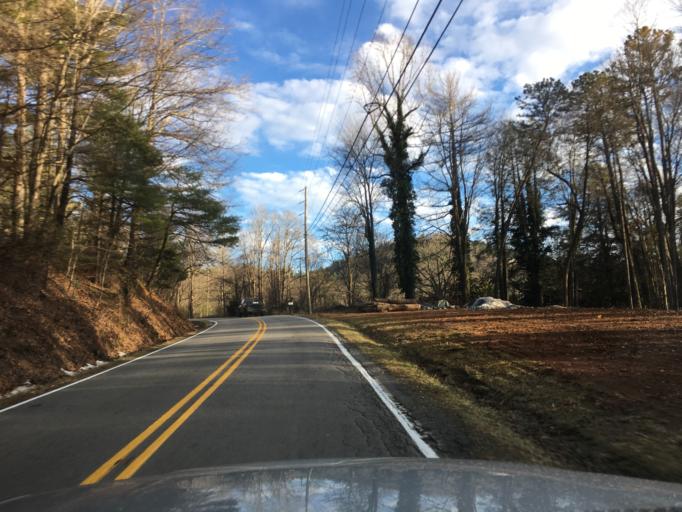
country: US
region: North Carolina
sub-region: Transylvania County
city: Brevard
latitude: 35.1107
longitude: -82.9714
